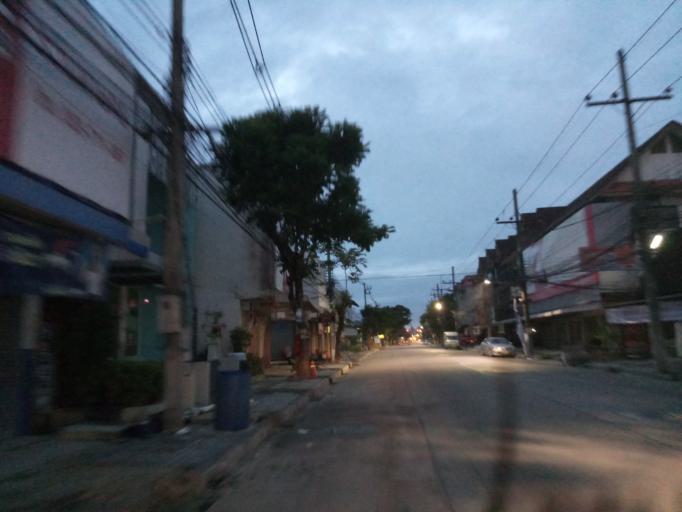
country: TH
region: Chiang Rai
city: Chiang Rai
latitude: 19.8985
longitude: 99.8322
